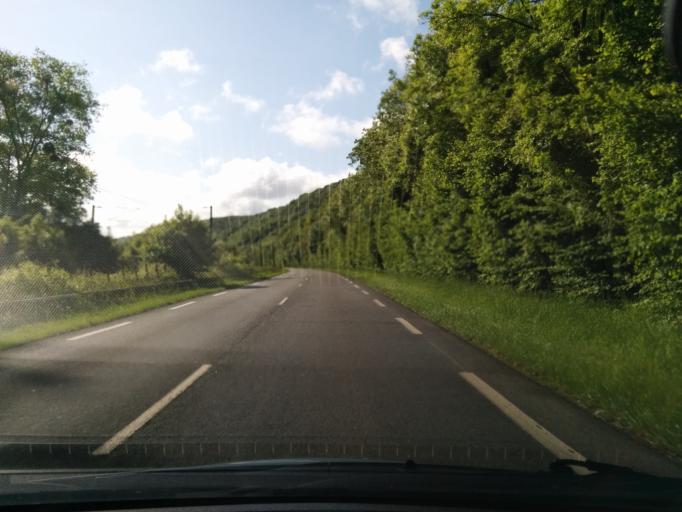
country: FR
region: Ile-de-France
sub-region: Departement des Yvelines
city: Bennecourt
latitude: 49.0416
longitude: 1.5352
